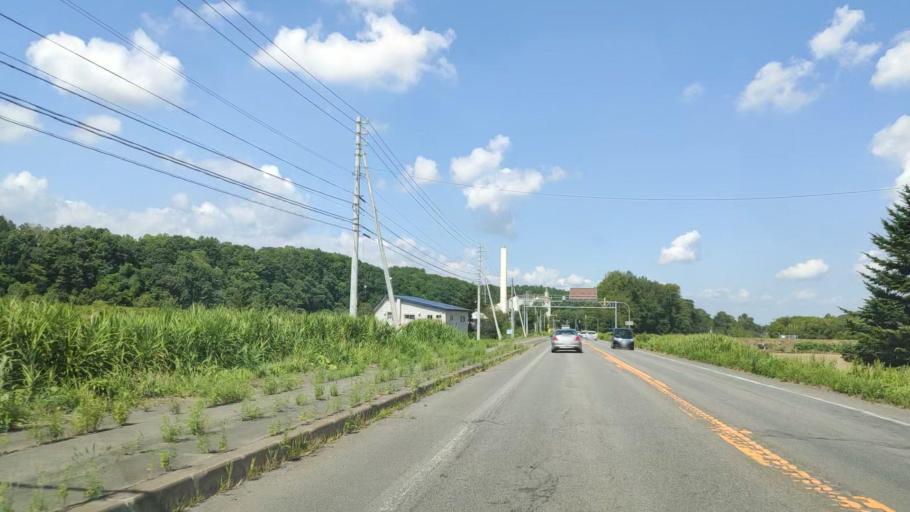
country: JP
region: Hokkaido
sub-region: Asahikawa-shi
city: Asahikawa
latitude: 43.6189
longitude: 142.4735
